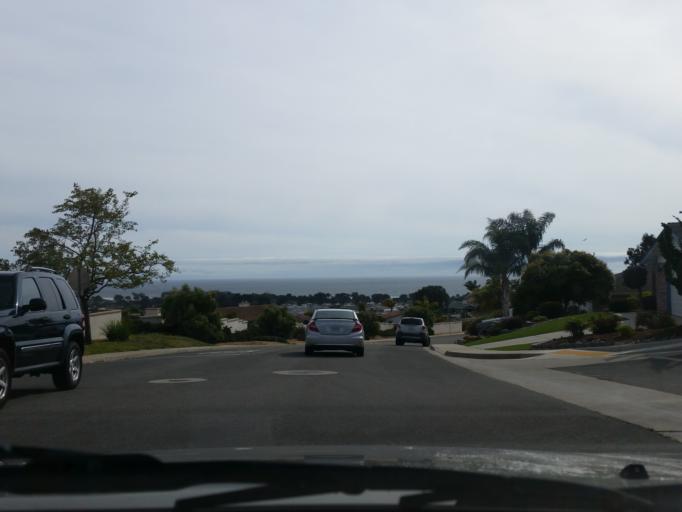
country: US
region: California
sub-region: San Luis Obispo County
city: Pismo Beach
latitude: 35.1414
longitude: -120.6262
